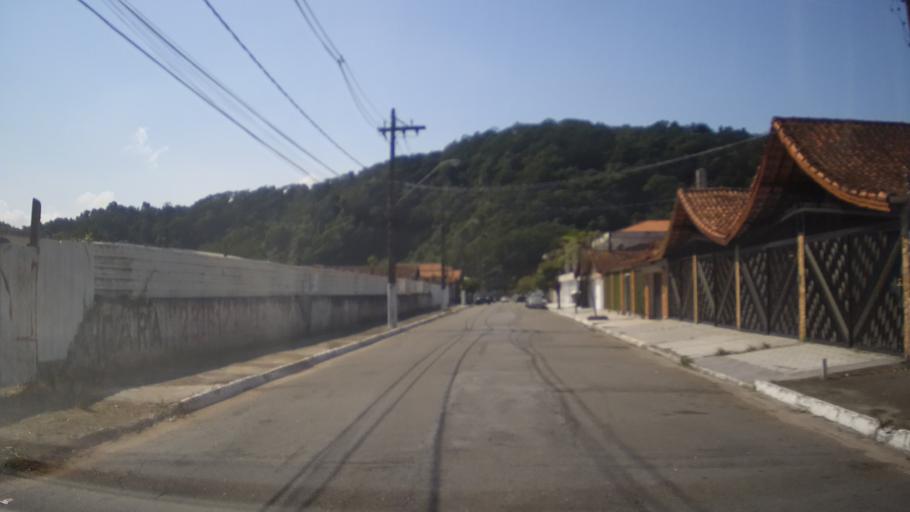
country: BR
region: Sao Paulo
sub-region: Praia Grande
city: Praia Grande
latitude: -24.0048
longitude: -46.4083
